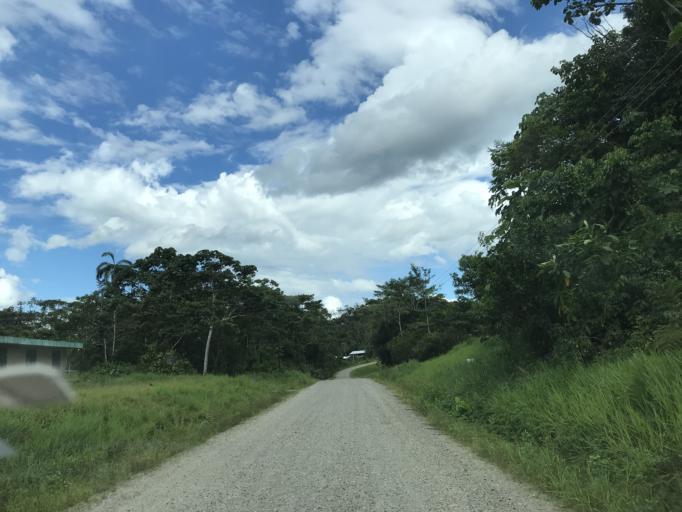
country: EC
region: Orellana
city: Puerto Francisco de Orellana
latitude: -0.6107
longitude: -76.4664
